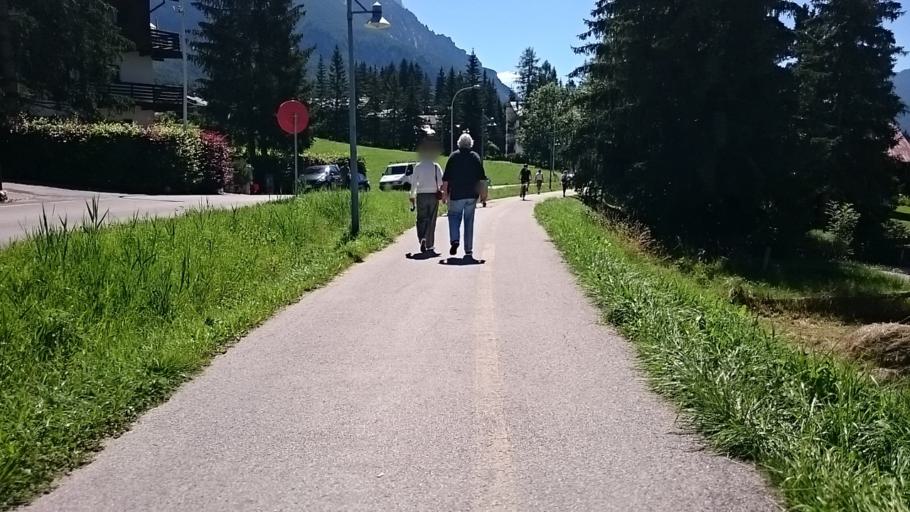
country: IT
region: Veneto
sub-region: Provincia di Belluno
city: Cortina d'Ampezzo
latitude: 46.5458
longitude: 12.1364
